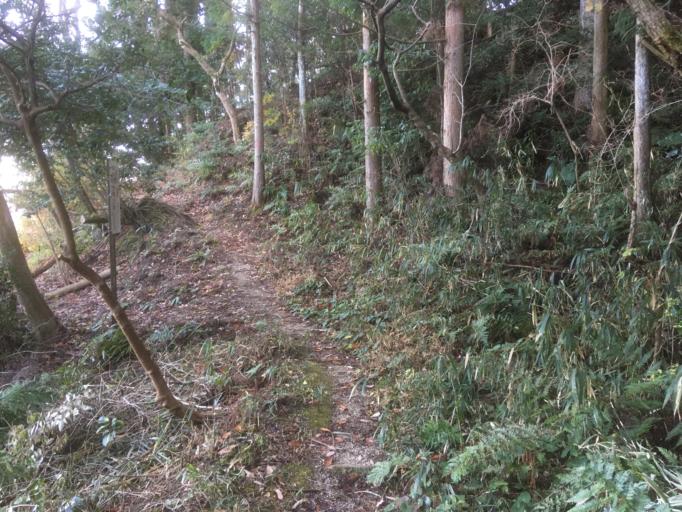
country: JP
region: Nara
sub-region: Ikoma-shi
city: Ikoma
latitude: 34.6984
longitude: 135.6850
